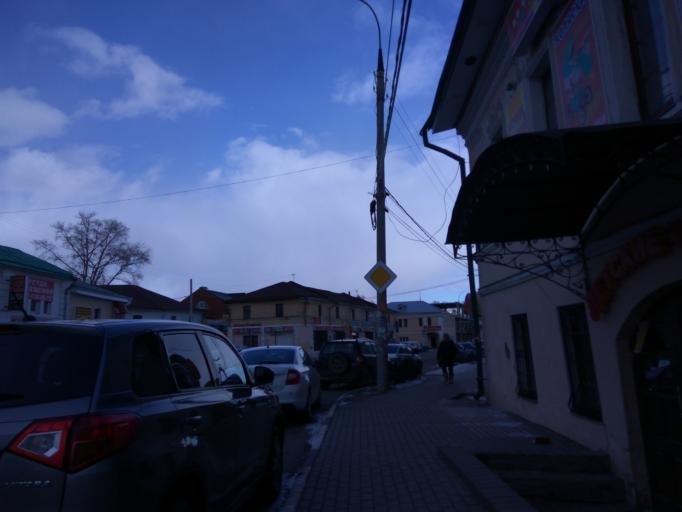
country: RU
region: Jaroslavl
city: Rostov
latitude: 57.1868
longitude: 39.4156
